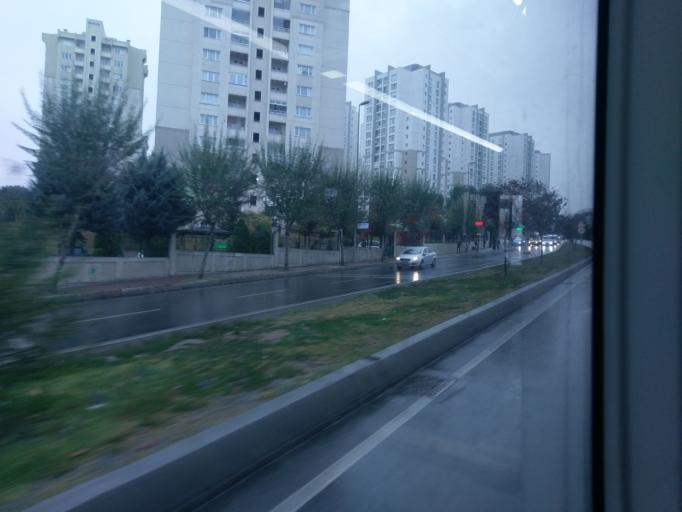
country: TR
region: Istanbul
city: Mahmutbey
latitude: 41.0337
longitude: 28.7733
